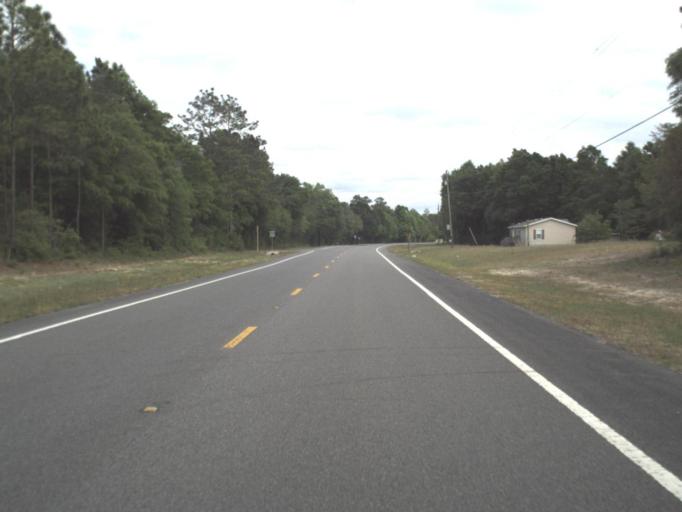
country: US
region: Florida
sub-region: Santa Rosa County
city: Point Baker
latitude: 30.6983
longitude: -87.0673
